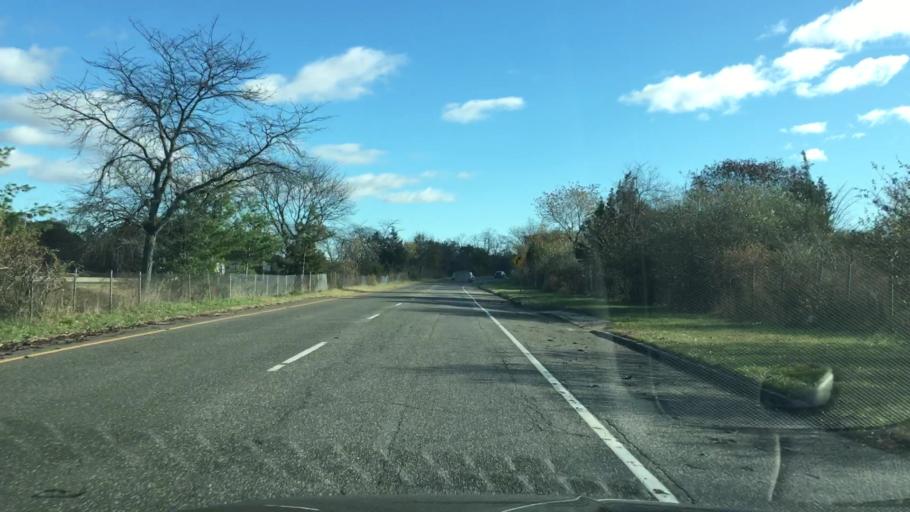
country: US
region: New York
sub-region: Suffolk County
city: Melville
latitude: 40.7835
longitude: -73.4002
